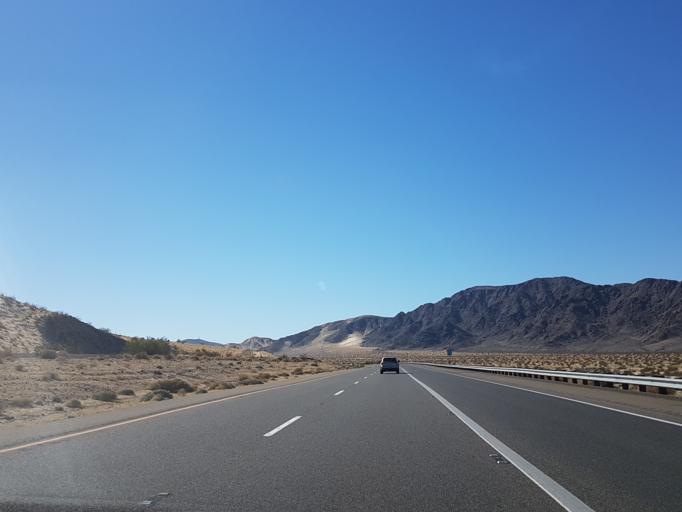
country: US
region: California
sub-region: San Bernardino County
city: Fort Irwin
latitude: 35.0990
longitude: -116.2881
